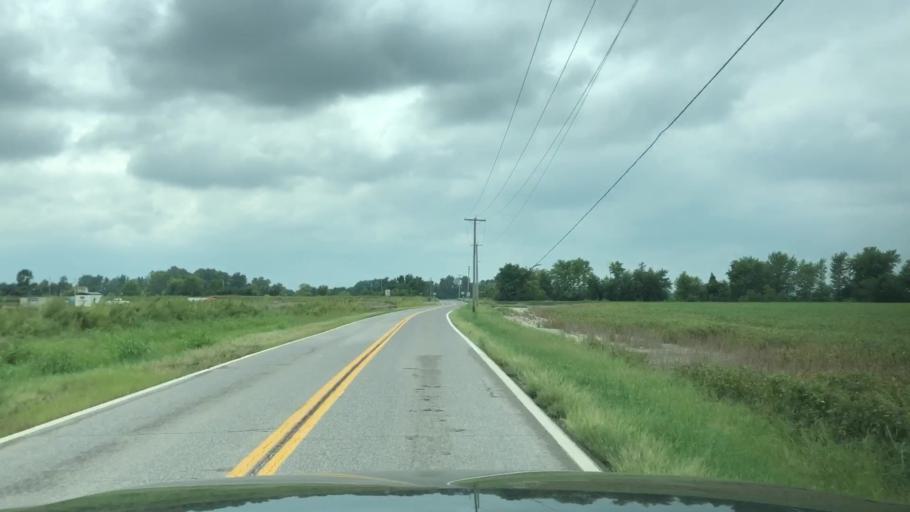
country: US
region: Missouri
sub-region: Saint Louis County
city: Bridgeton
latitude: 38.8018
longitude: -90.4088
